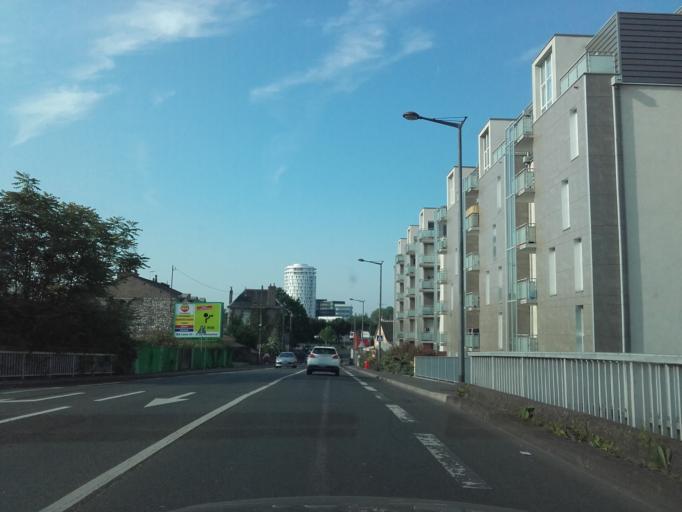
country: FR
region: Centre
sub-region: Departement d'Indre-et-Loire
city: Tours
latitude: 47.3755
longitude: 0.6790
